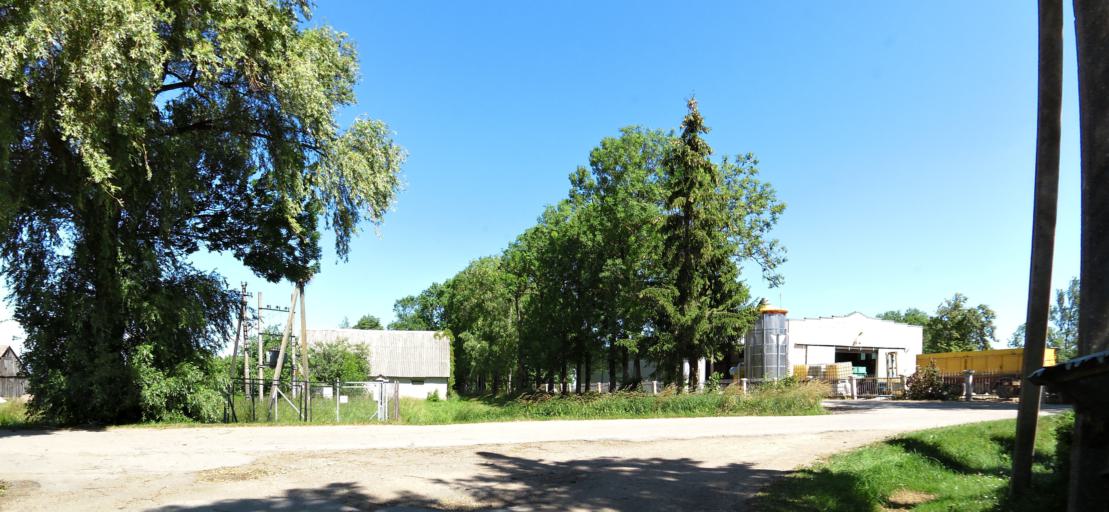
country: LT
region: Panevezys
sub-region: Birzai
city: Birzai
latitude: 56.2533
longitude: 24.5393
